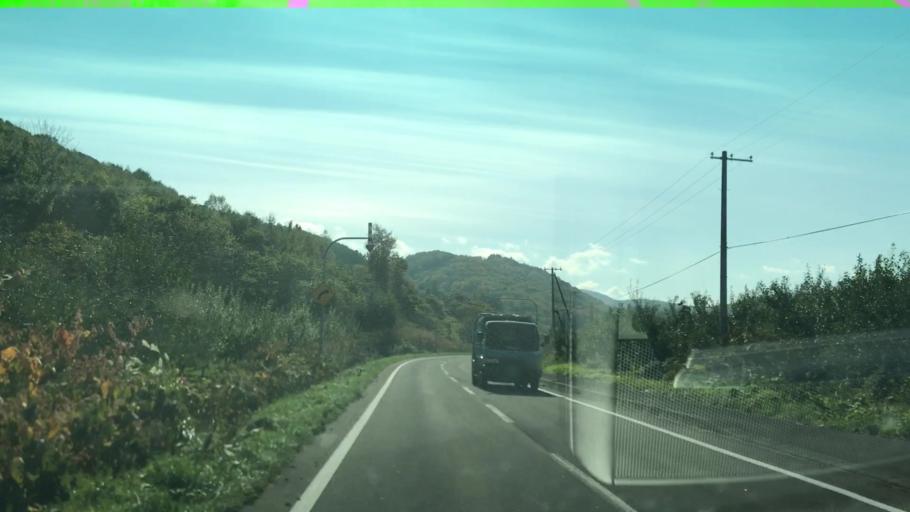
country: JP
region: Hokkaido
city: Yoichi
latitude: 43.1609
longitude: 140.8215
